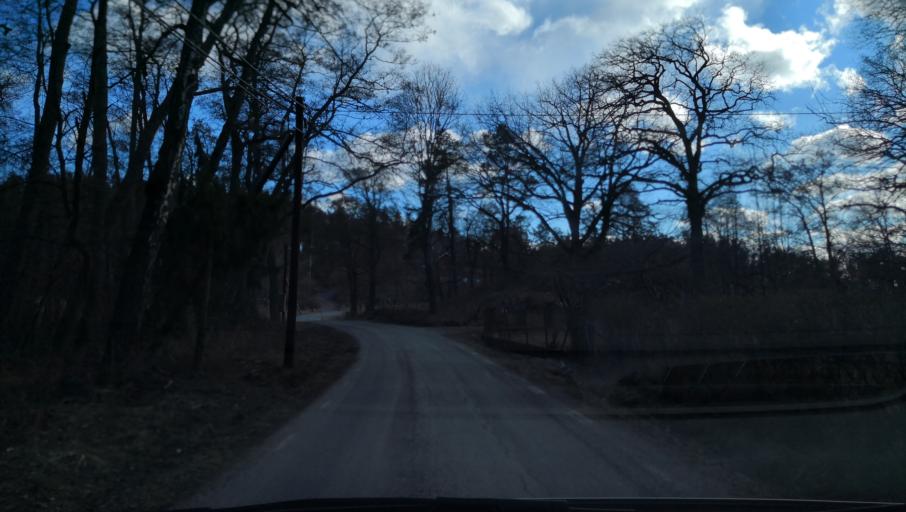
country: SE
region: Stockholm
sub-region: Varmdo Kommun
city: Mortnas
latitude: 59.3894
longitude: 18.4544
